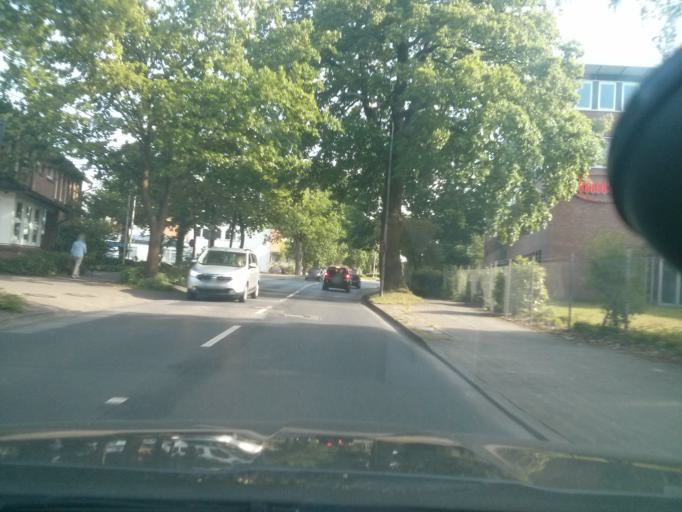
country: DE
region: Schleswig-Holstein
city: Halstenbek
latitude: 53.6046
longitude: 9.8362
